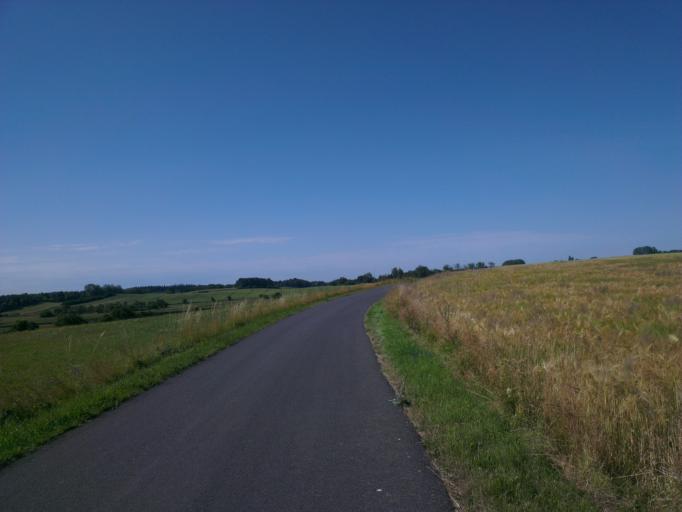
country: DK
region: Zealand
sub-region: Roskilde Kommune
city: Jyllinge
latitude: 55.7606
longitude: 12.0521
